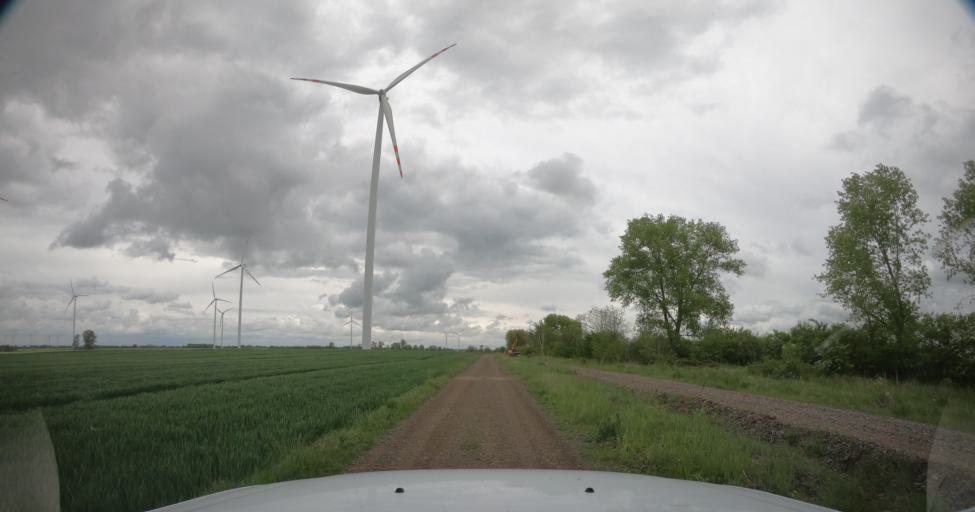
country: PL
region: West Pomeranian Voivodeship
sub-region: Powiat pyrzycki
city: Kozielice
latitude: 53.1025
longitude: 14.8038
